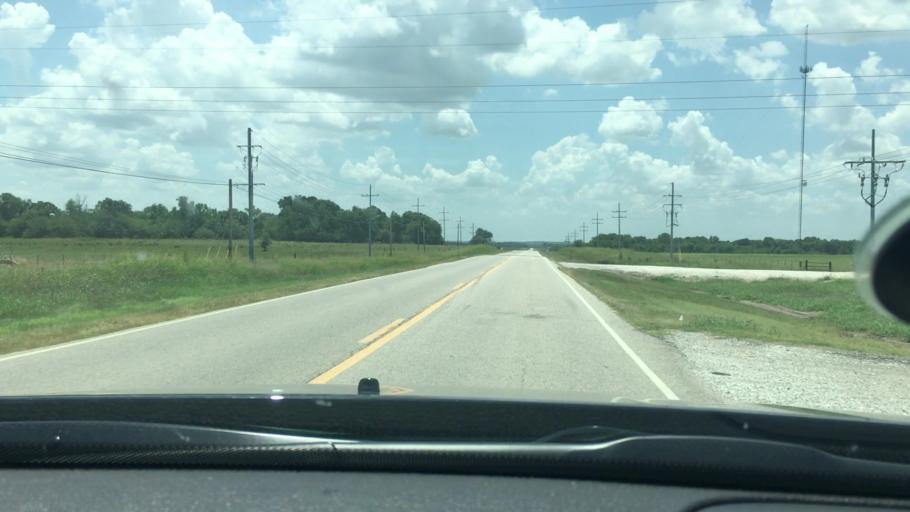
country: US
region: Oklahoma
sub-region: Pontotoc County
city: Ada
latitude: 34.6554
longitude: -96.6349
